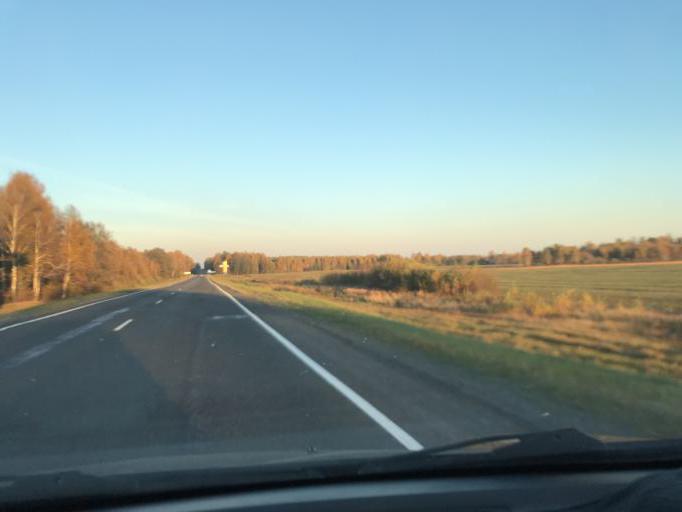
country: BY
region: Mogilev
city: Hlusk
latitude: 53.0644
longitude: 28.5273
